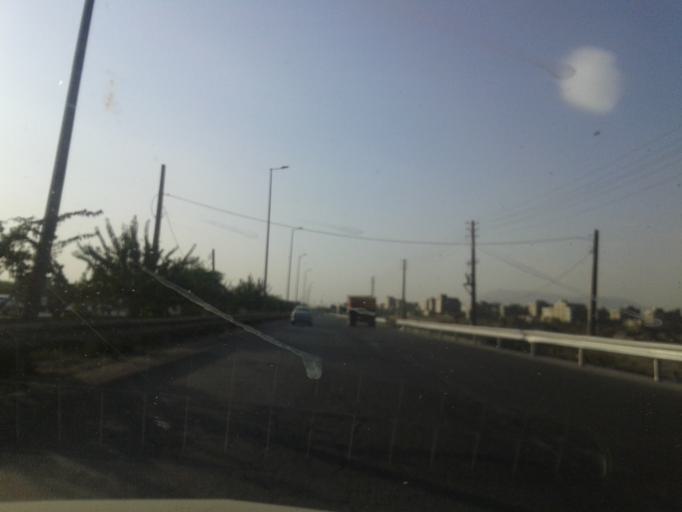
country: IR
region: Tehran
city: Eslamshahr
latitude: 35.6509
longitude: 51.2728
